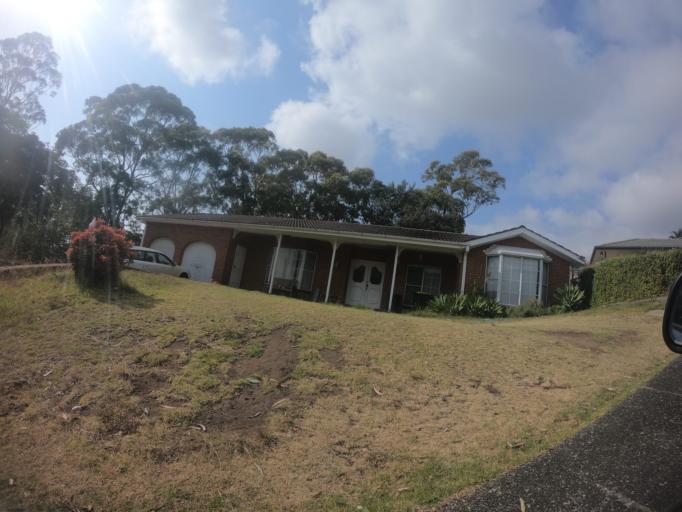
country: AU
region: New South Wales
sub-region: Wollongong
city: Bulli
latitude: -34.3201
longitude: 150.9100
